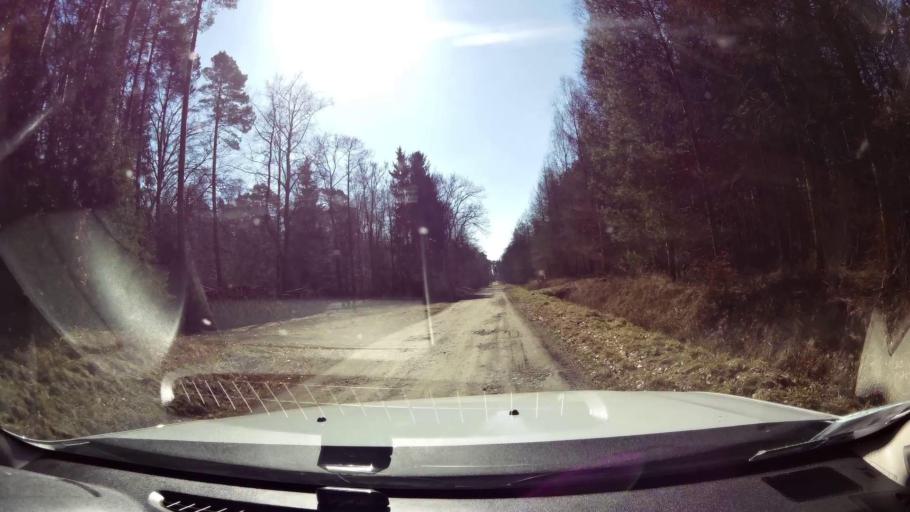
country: PL
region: West Pomeranian Voivodeship
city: Trzcinsko Zdroj
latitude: 53.0054
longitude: 14.6141
